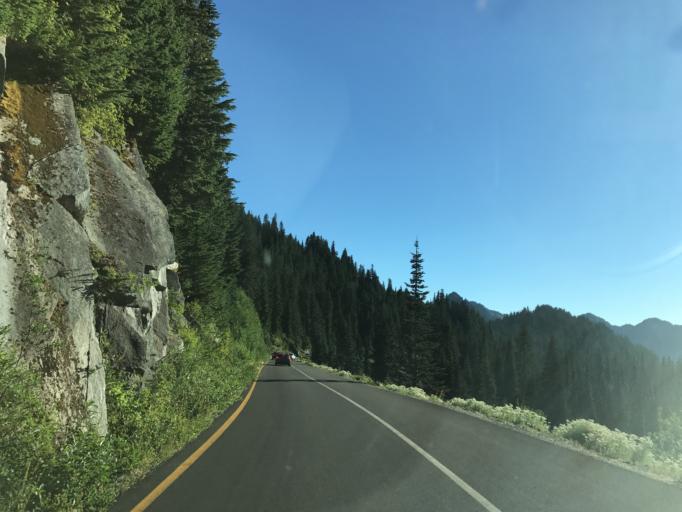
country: US
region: Washington
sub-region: Pierce County
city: Buckley
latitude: 46.7829
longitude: -121.7275
